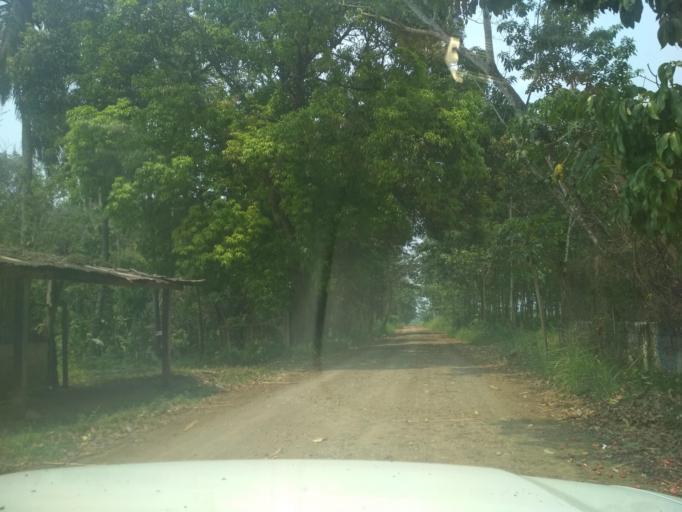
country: MX
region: Veracruz
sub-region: Tezonapa
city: Laguna Chica (Pueblo Nuevo)
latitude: 18.5121
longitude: -96.7668
